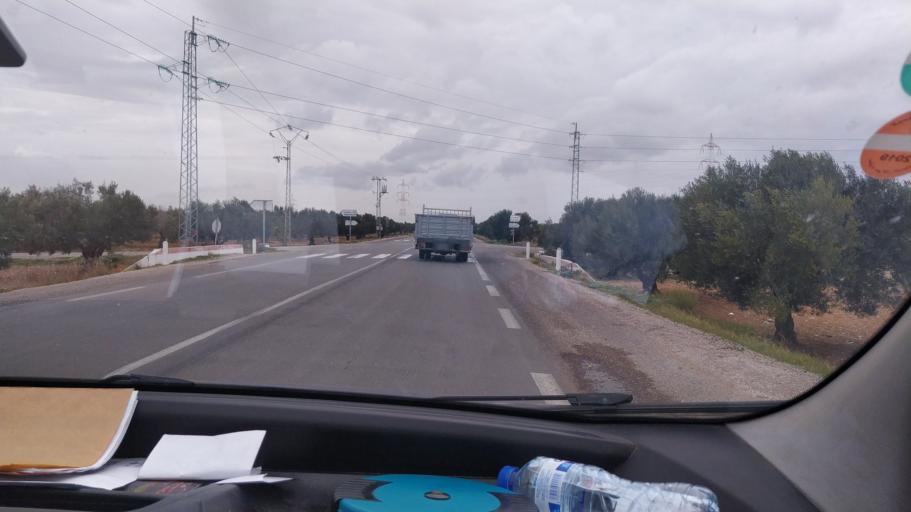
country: TN
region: Al Munastir
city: Sidi Bin Nur
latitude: 35.4848
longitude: 10.9434
